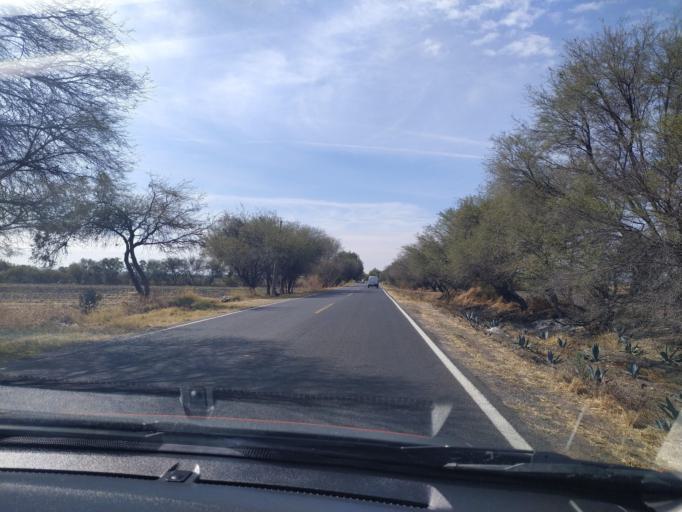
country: MX
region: Guanajuato
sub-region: San Francisco del Rincon
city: San Ignacio de Hidalgo
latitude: 20.9210
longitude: -101.8553
